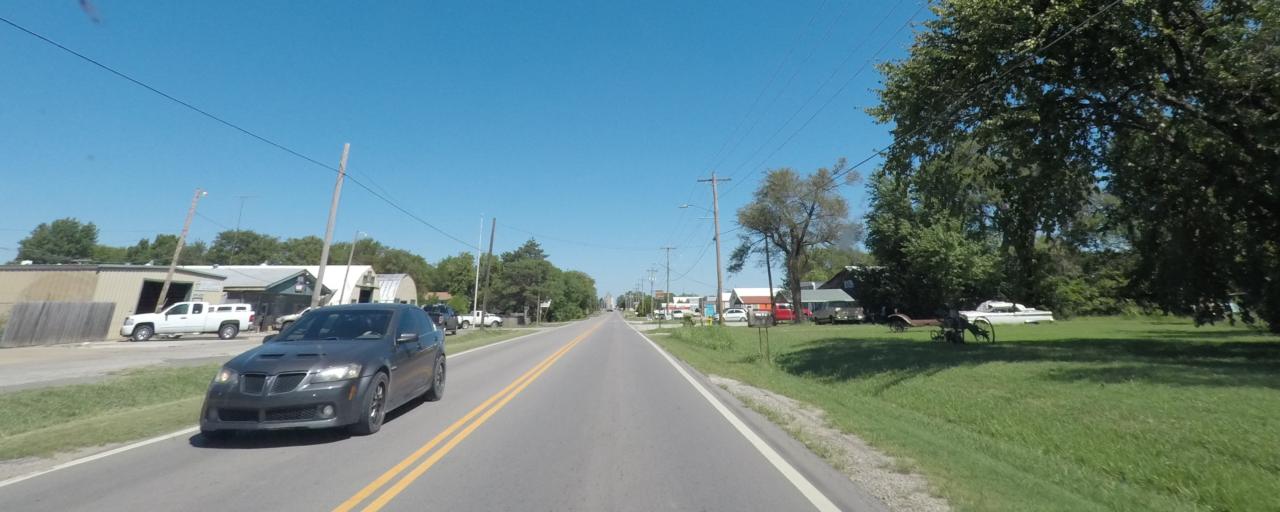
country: US
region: Kansas
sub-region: Sumner County
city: Wellington
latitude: 37.2840
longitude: -97.3943
